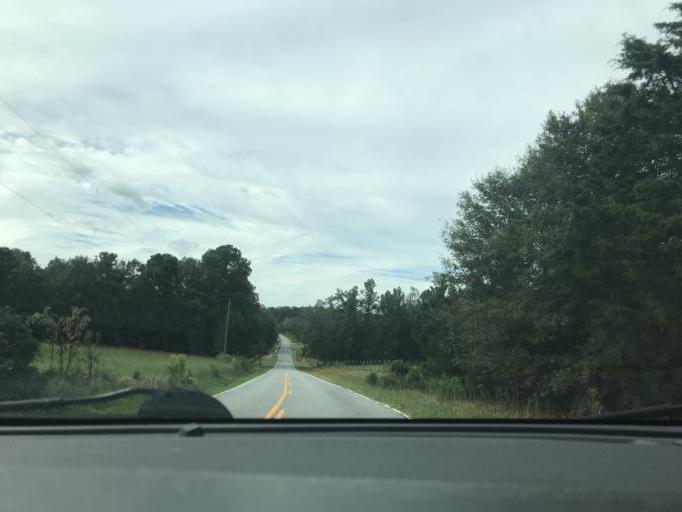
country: US
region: South Carolina
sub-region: Cherokee County
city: Gaffney
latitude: 35.1405
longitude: -81.6915
